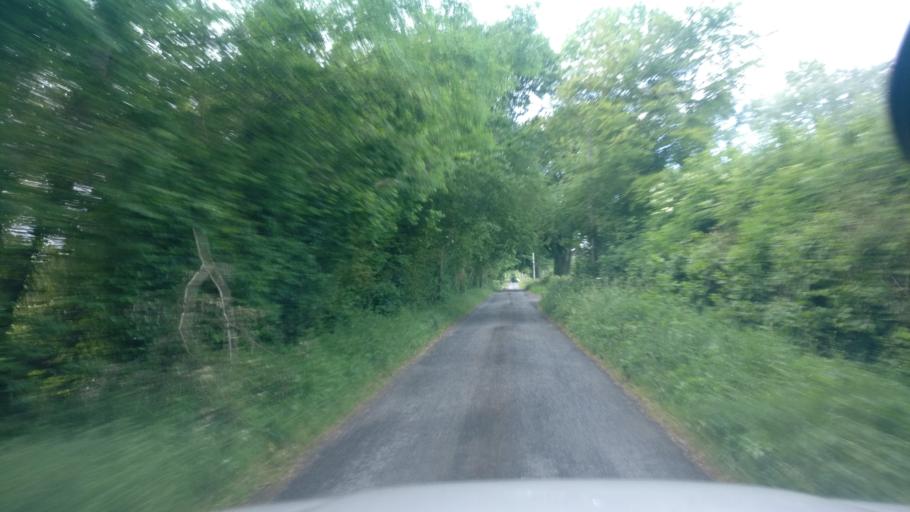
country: IE
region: Connaught
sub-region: County Galway
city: Ballinasloe
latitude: 53.2299
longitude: -8.2285
